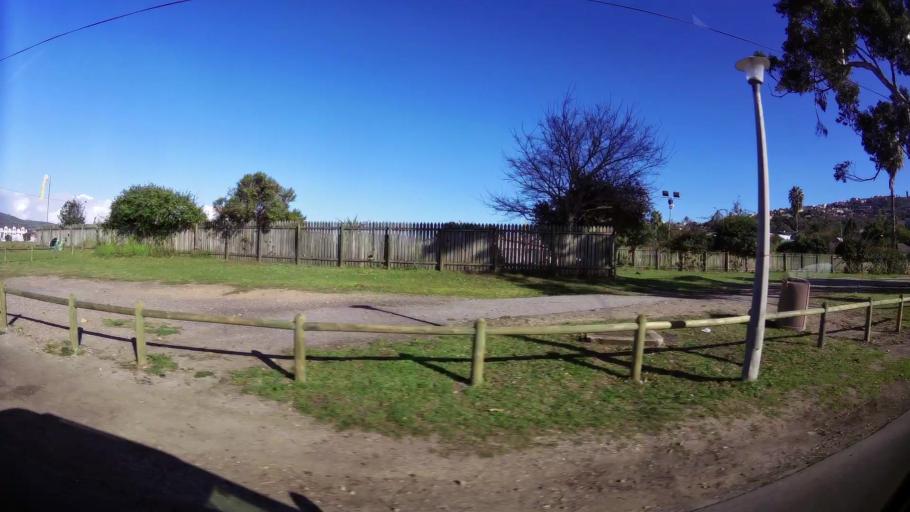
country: ZA
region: Western Cape
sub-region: Eden District Municipality
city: Knysna
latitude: -34.0372
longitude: 23.0435
